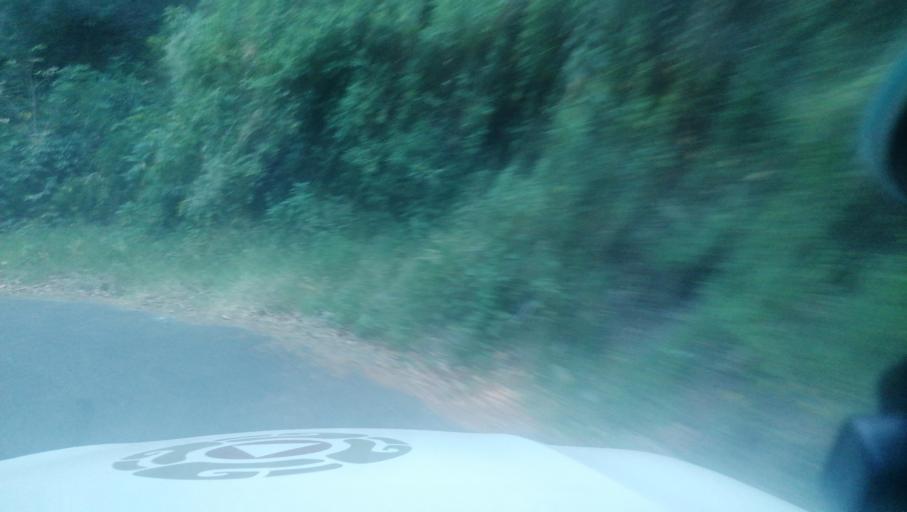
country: MX
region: Chiapas
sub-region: Cacahoatan
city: Benito Juarez
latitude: 15.1419
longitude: -92.1950
